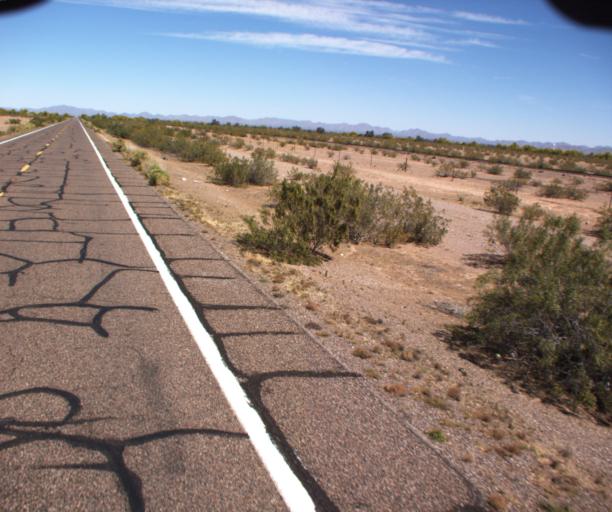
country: US
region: Arizona
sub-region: Maricopa County
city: Gila Bend
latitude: 32.8723
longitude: -112.7589
